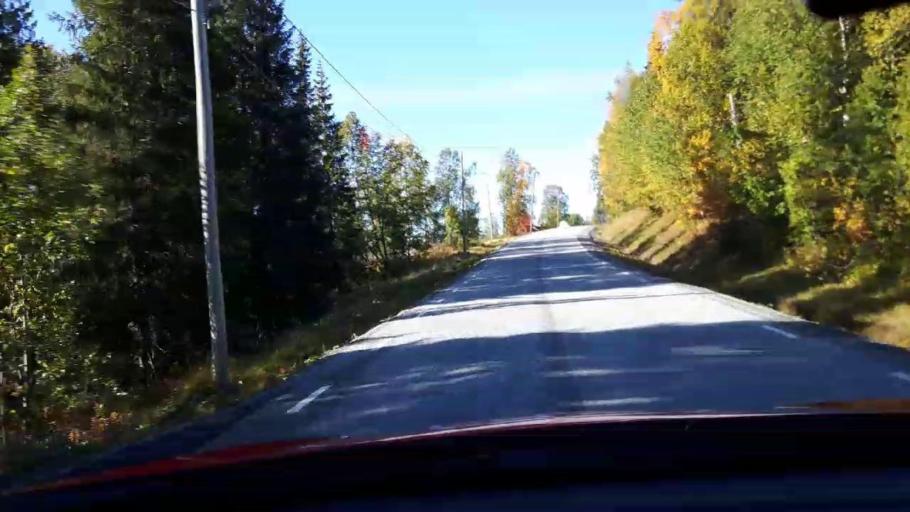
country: NO
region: Nord-Trondelag
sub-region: Royrvik
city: Royrvik
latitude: 64.8285
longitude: 14.1218
